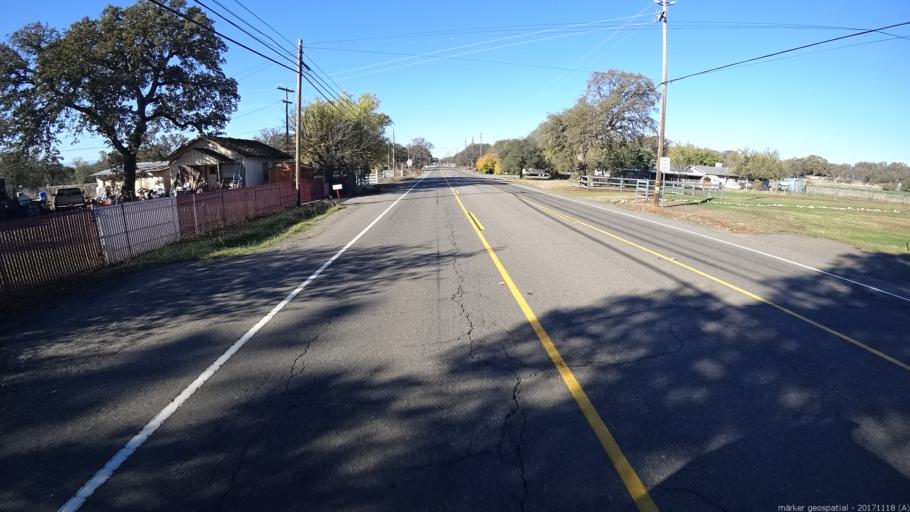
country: US
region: California
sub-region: Shasta County
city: Cottonwood
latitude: 40.3892
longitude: -122.3170
